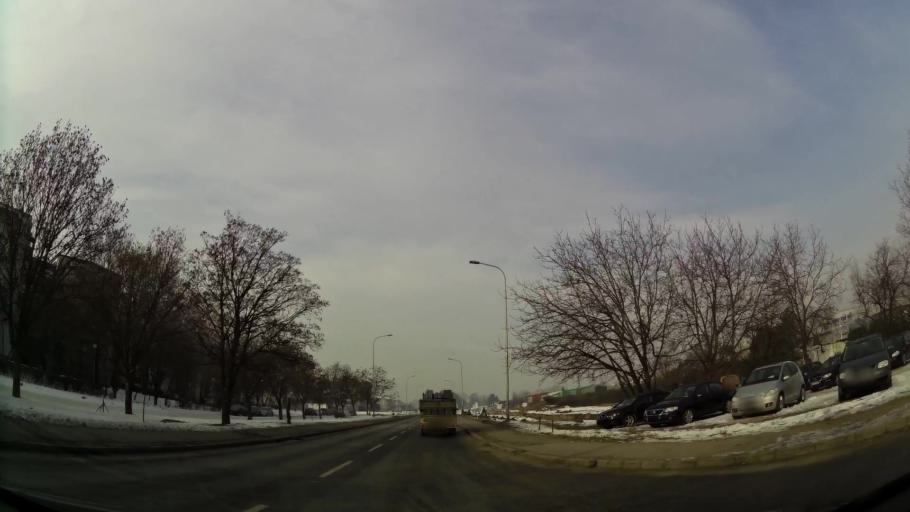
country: MK
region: Butel
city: Butel
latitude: 42.0251
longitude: 21.4395
